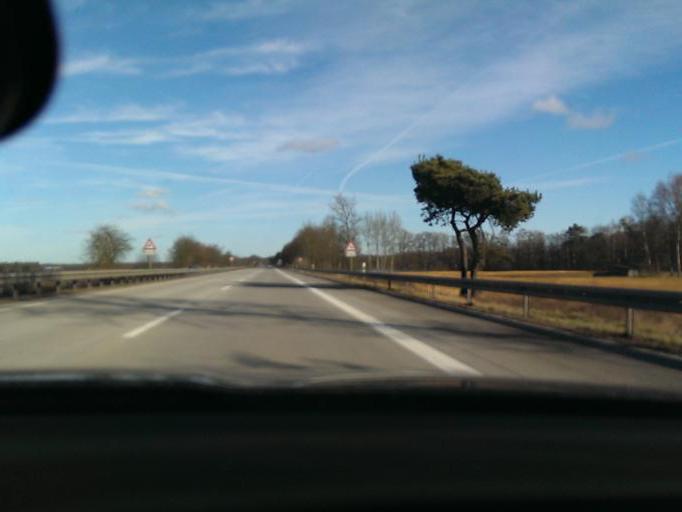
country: DE
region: Lower Saxony
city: Elze
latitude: 52.5347
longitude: 9.7928
